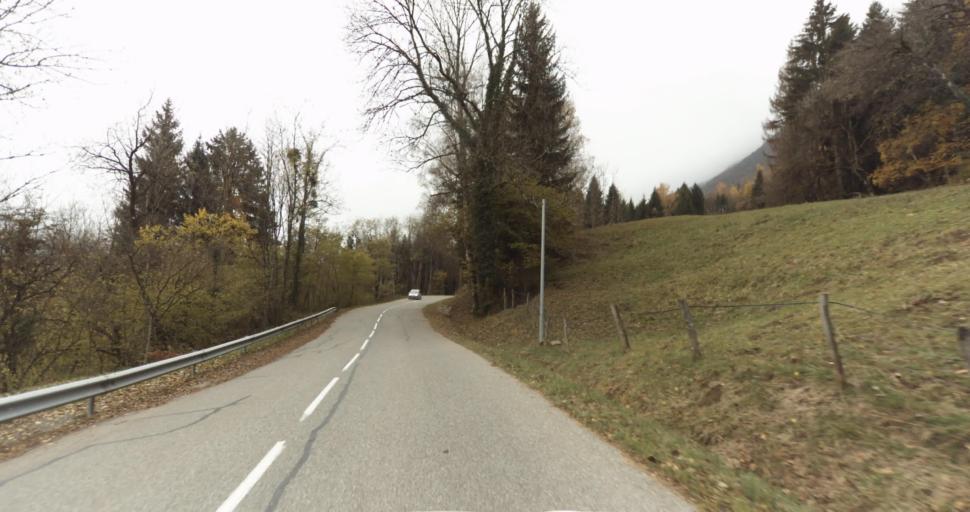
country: FR
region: Rhone-Alpes
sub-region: Departement de la Haute-Savoie
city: Saint-Jorioz
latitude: 45.8234
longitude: 6.1366
